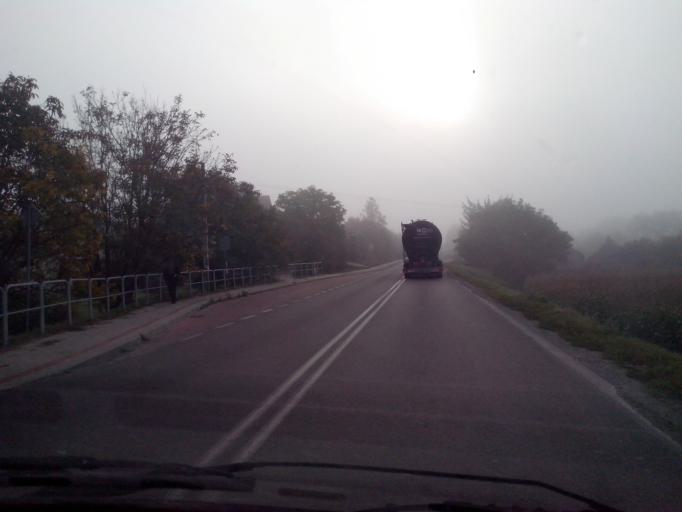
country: PL
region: Subcarpathian Voivodeship
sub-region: Powiat przemyski
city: Krasiczyn
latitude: 49.8081
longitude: 22.7004
